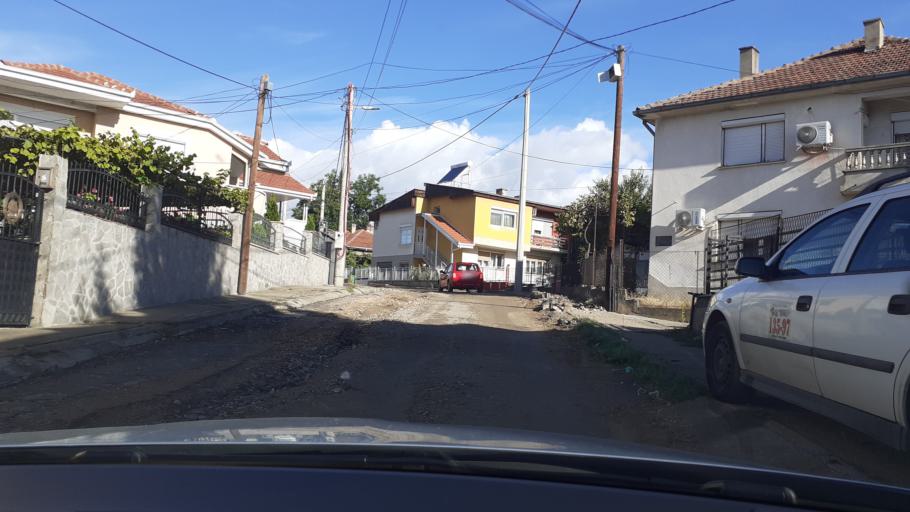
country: MK
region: Kocani
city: Kochani
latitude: 41.9127
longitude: 22.4176
